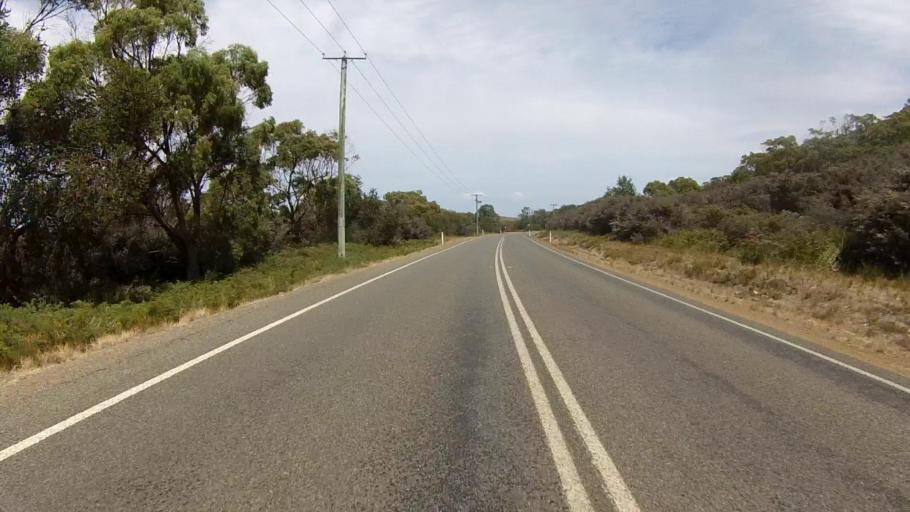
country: AU
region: Tasmania
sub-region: Clarence
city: Sandford
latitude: -43.0221
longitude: 147.4876
